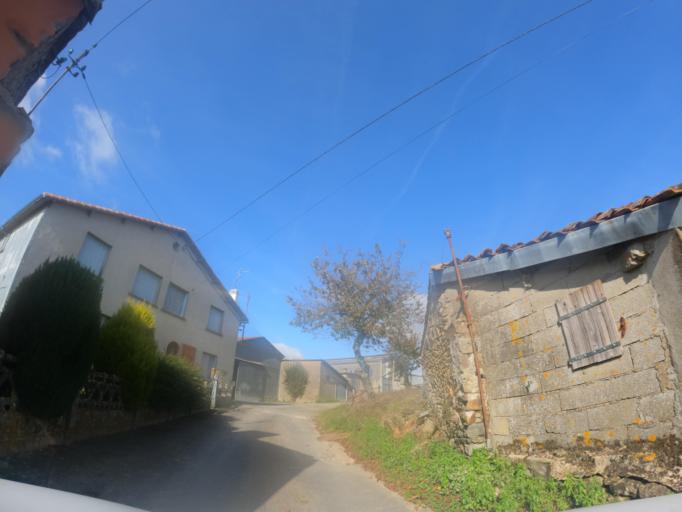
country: FR
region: Poitou-Charentes
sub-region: Departement des Deux-Sevres
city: Courlay
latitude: 46.7844
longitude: -0.5879
